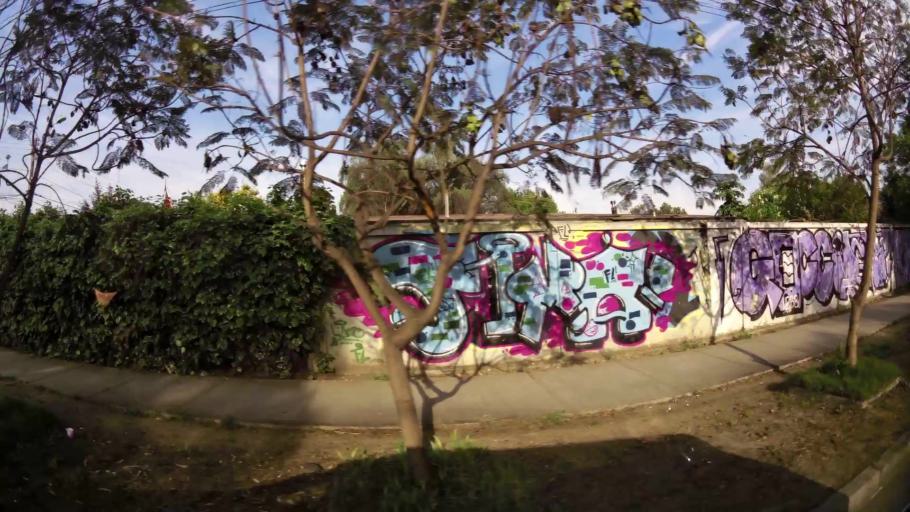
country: CL
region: Santiago Metropolitan
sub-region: Provincia de Talagante
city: Talagante
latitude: -33.6646
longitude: -70.9333
